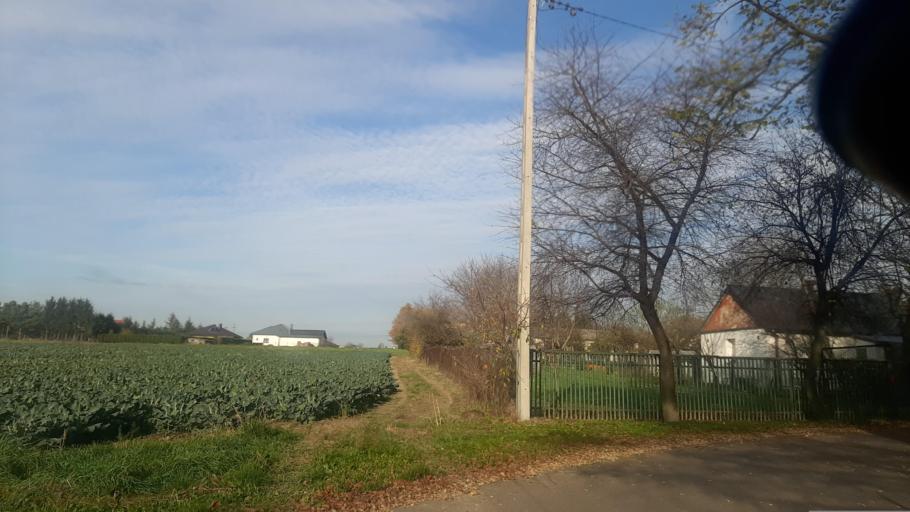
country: PL
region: Lublin Voivodeship
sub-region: Powiat pulawski
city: Markuszow
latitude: 51.3609
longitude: 22.2895
